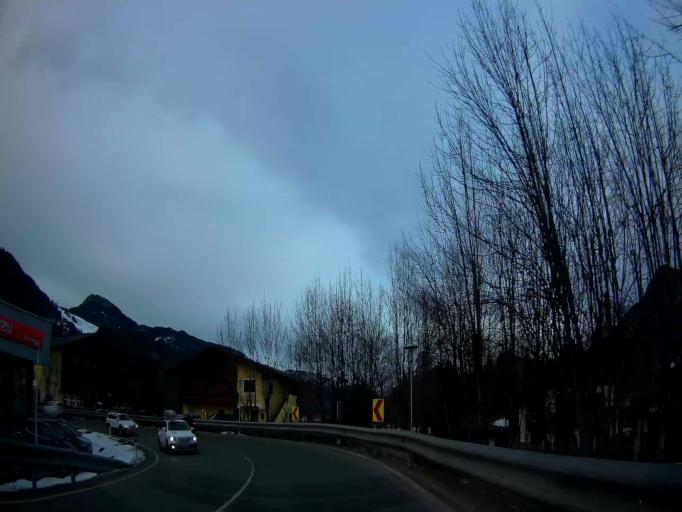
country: AT
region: Salzburg
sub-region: Politischer Bezirk Zell am See
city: Lofer
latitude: 47.5940
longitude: 12.7005
